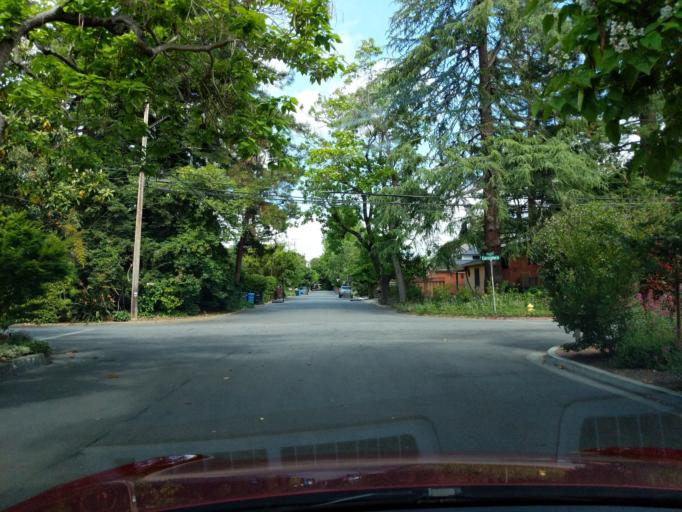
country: US
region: California
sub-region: San Mateo County
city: Menlo Park
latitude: 37.4427
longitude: -122.1784
